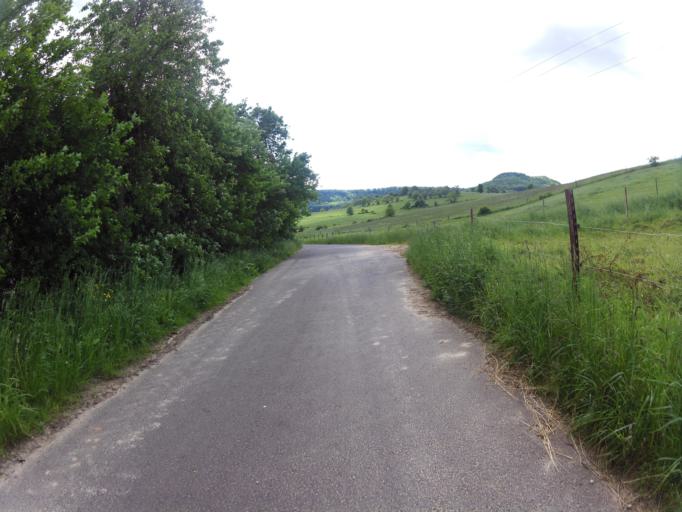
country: DE
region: Thuringia
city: Treffurt
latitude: 51.1122
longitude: 10.2214
